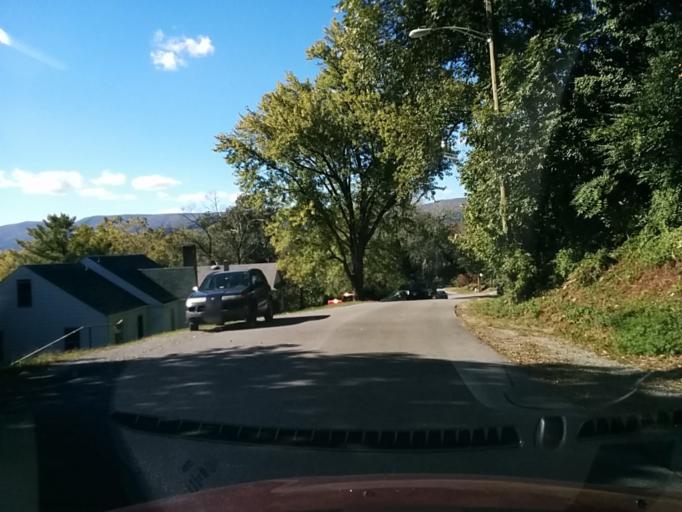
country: US
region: Virginia
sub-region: City of Salem
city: Salem
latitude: 37.2889
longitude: -80.0494
